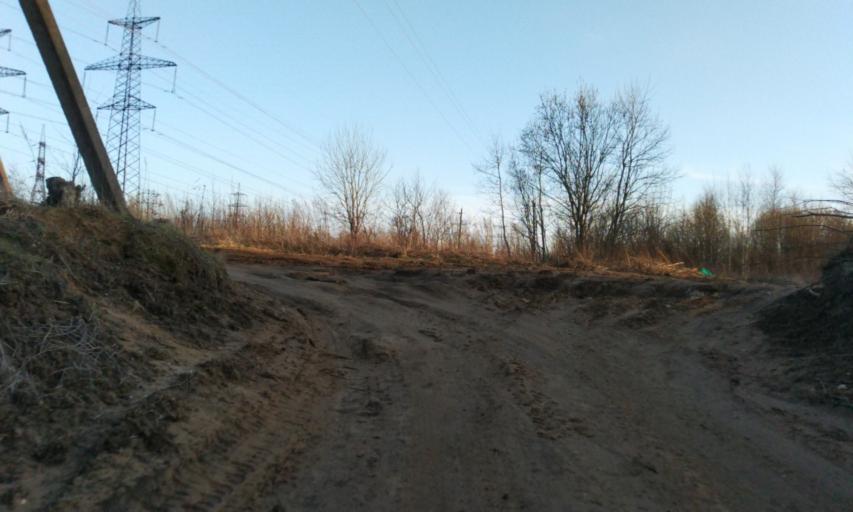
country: RU
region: Leningrad
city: Novoye Devyatkino
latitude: 60.0839
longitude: 30.4591
